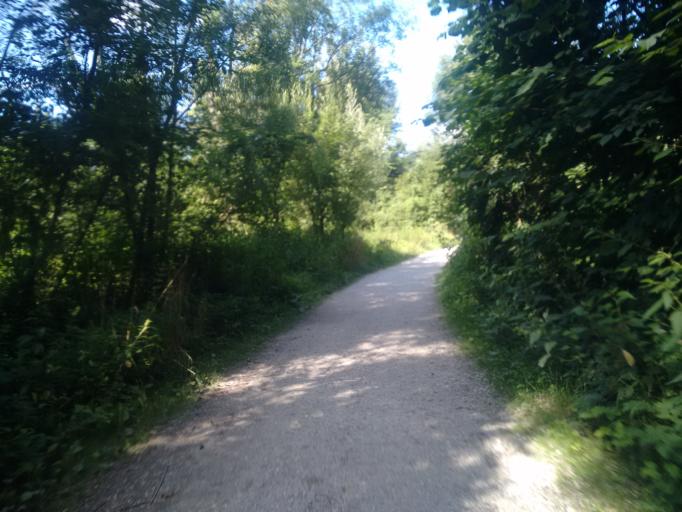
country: AT
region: Upper Austria
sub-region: Wels-Land
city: Thalheim bei Wels
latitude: 48.1455
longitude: 14.0142
